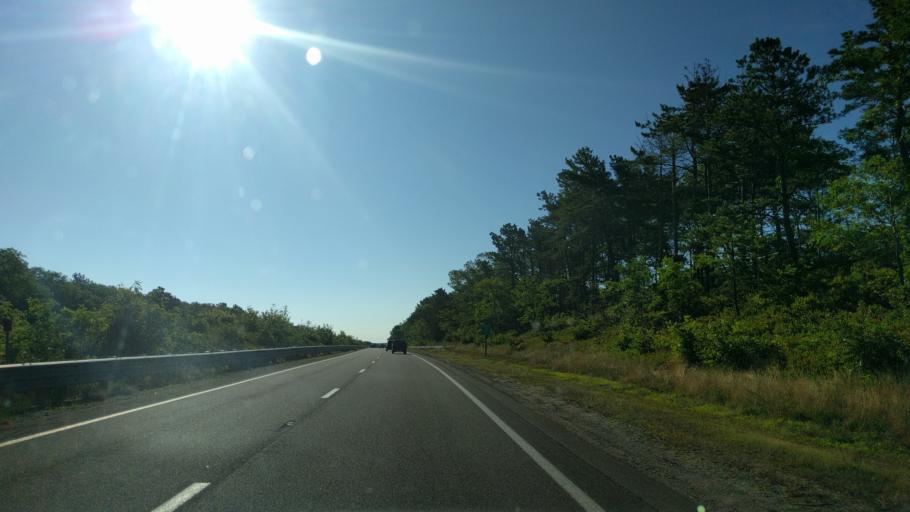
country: US
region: Massachusetts
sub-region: Barnstable County
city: East Sandwich
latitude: 41.7294
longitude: -70.4525
